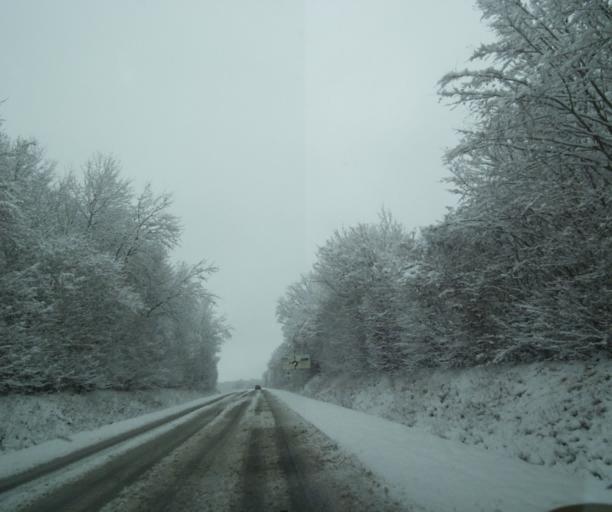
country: FR
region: Champagne-Ardenne
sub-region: Departement de la Haute-Marne
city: Saint-Dizier
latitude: 48.6024
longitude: 4.9101
